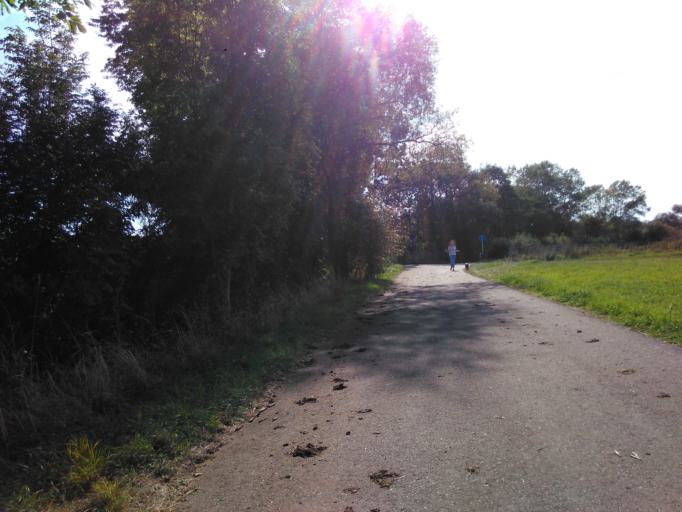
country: LU
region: Luxembourg
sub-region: Canton de Capellen
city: Bascharage
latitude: 49.5622
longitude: 5.8972
